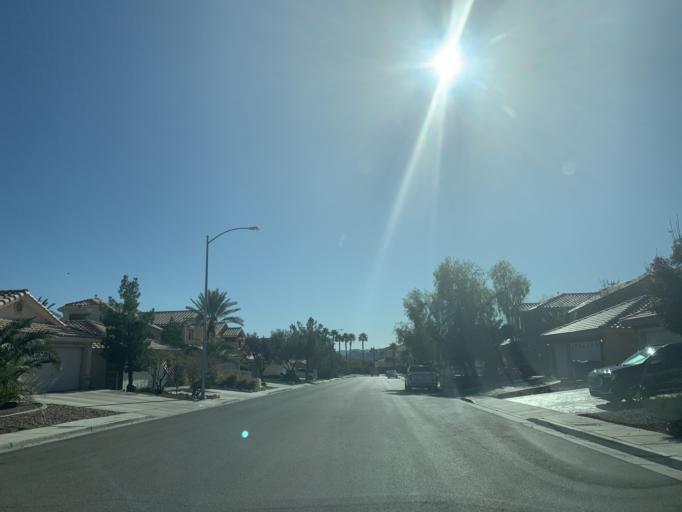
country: US
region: Nevada
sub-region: Clark County
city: Summerlin South
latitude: 36.1220
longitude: -115.3067
